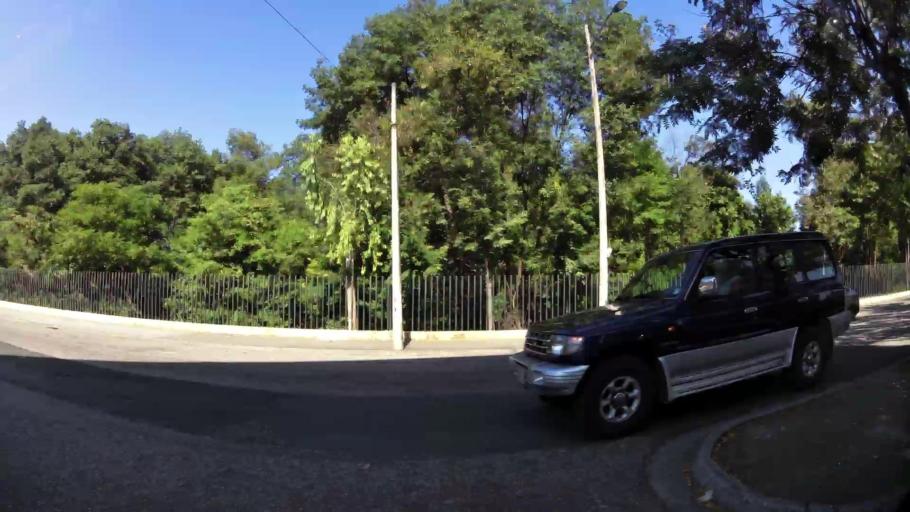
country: EC
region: Guayas
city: Guayaquil
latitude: -2.1635
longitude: -79.9008
